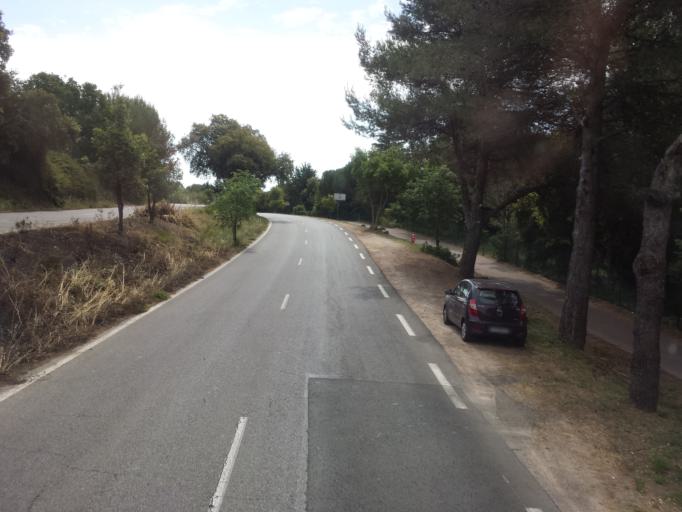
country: FR
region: Provence-Alpes-Cote d'Azur
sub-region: Departement des Alpes-Maritimes
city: Biot
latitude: 43.6159
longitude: 7.0777
